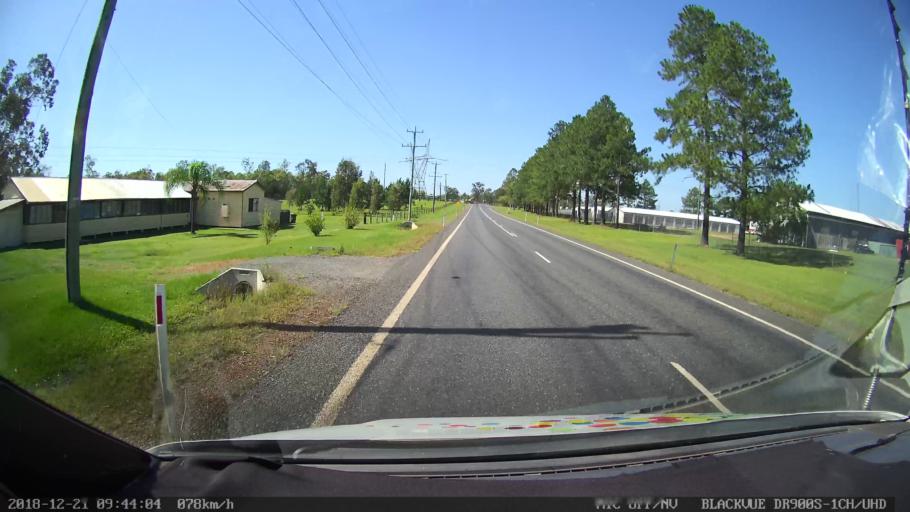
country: AU
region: New South Wales
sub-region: Clarence Valley
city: Grafton
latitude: -29.6138
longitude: 152.9346
